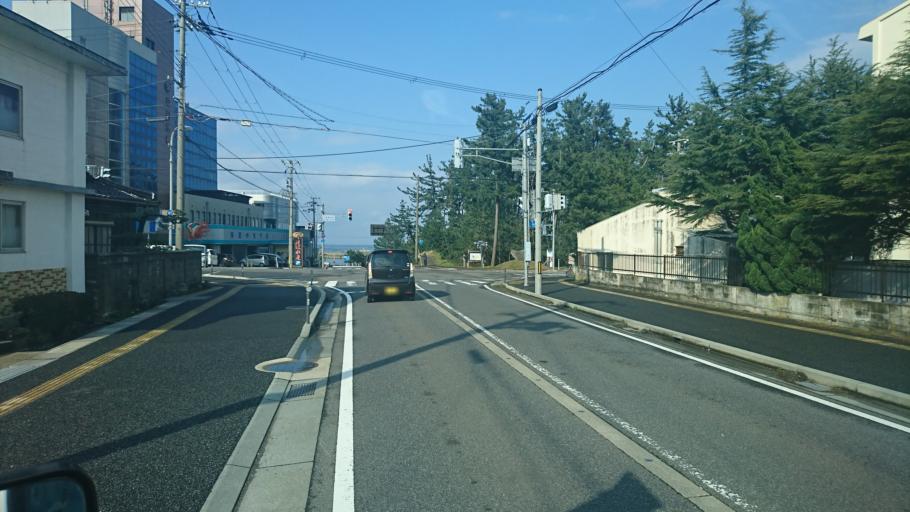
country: JP
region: Tottori
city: Tottori
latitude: 35.6267
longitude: 134.4453
